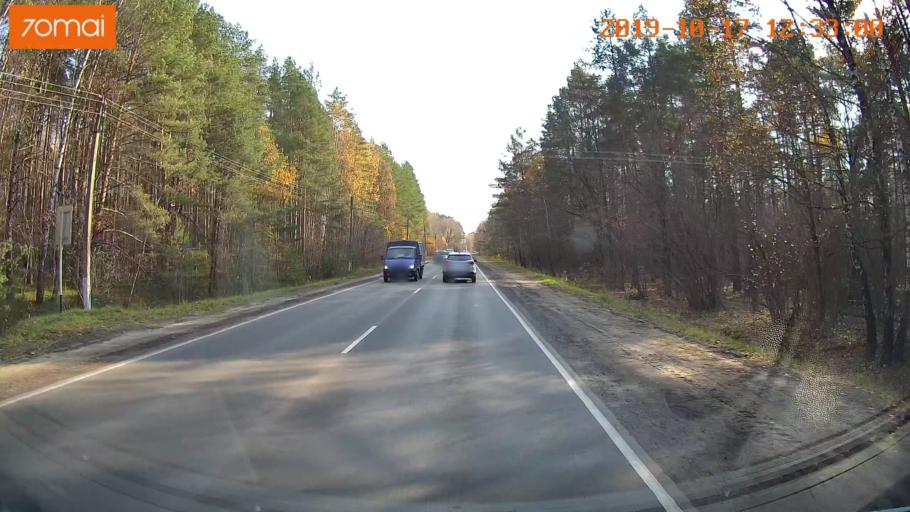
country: RU
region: Rjazan
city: Kasimov
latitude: 54.9582
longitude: 41.3490
